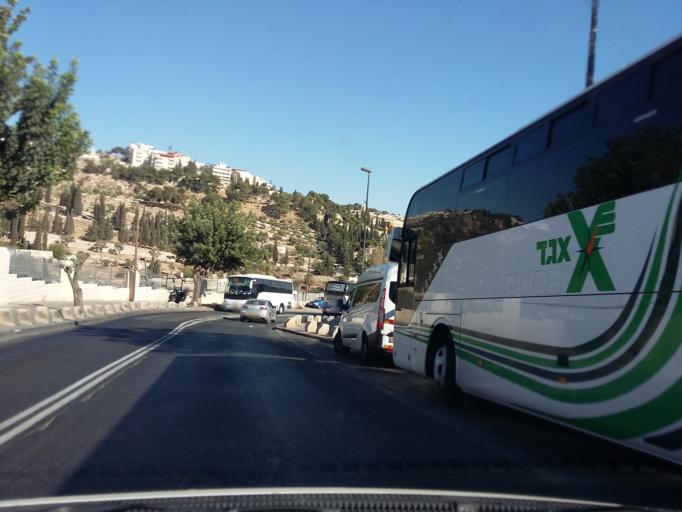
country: PS
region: West Bank
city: East Jerusalem
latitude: 31.7823
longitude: 35.2388
